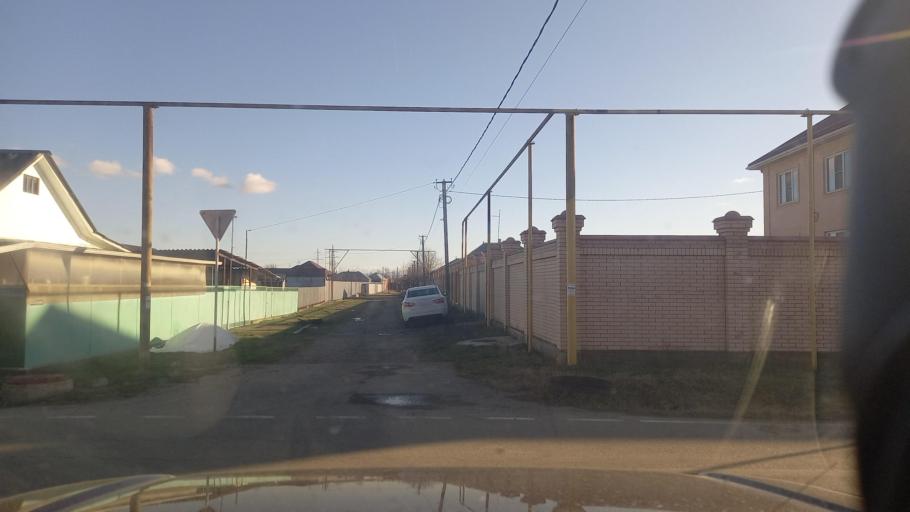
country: RU
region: Adygeya
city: Yablonovskiy
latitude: 45.0287
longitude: 38.8944
